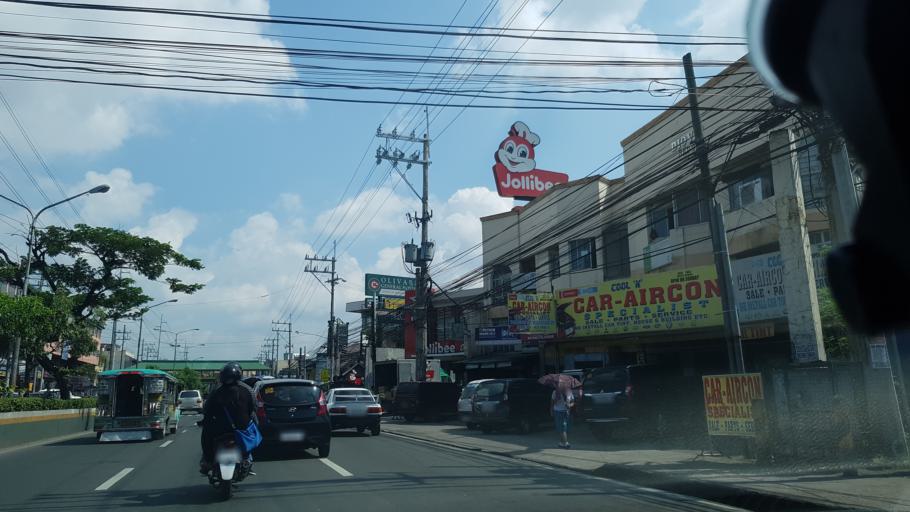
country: PH
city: Sambayanihan People's Village
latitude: 14.4800
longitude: 120.9973
